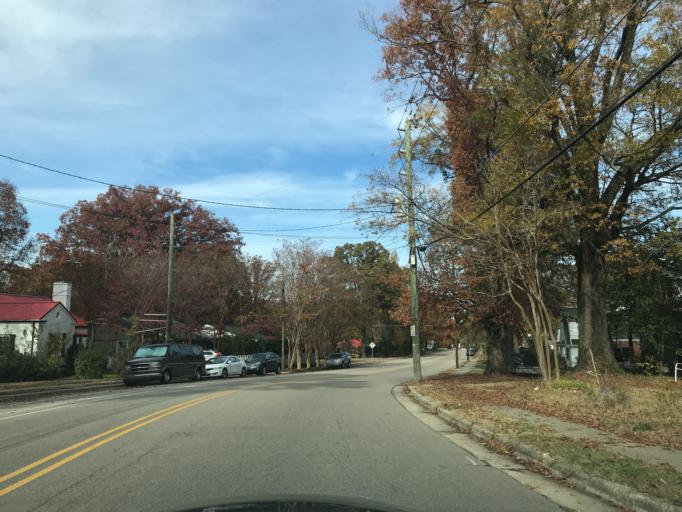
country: US
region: North Carolina
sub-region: Wake County
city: West Raleigh
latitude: 35.7976
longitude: -78.6766
